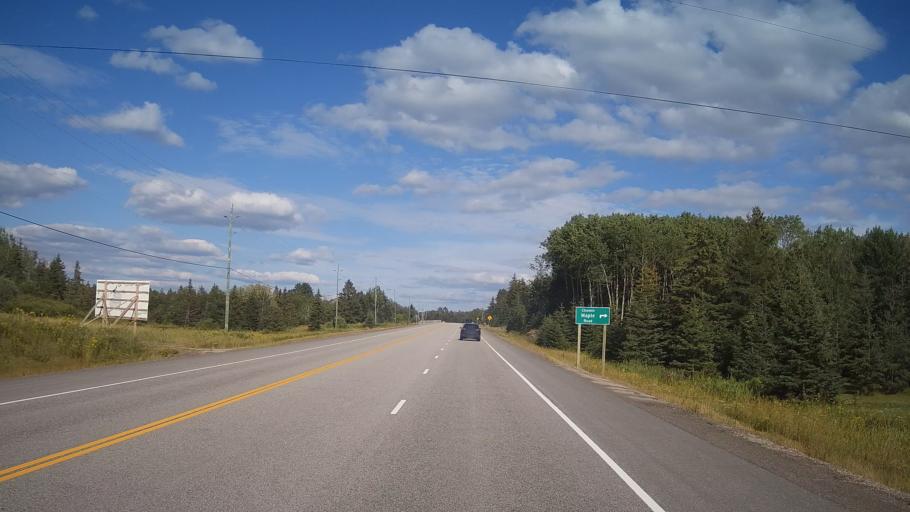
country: CA
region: Ontario
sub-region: Nipissing District
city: North Bay
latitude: 46.2681
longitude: -79.1990
